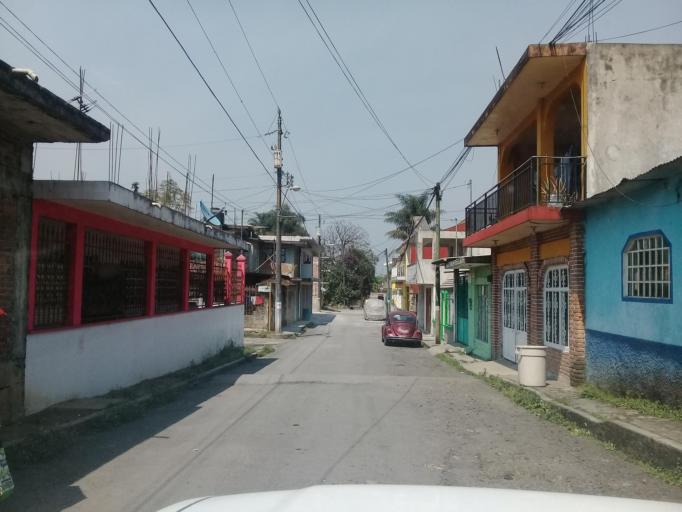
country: MX
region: Veracruz
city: Ixtac Zoquitlan
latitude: 18.8728
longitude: -97.0582
